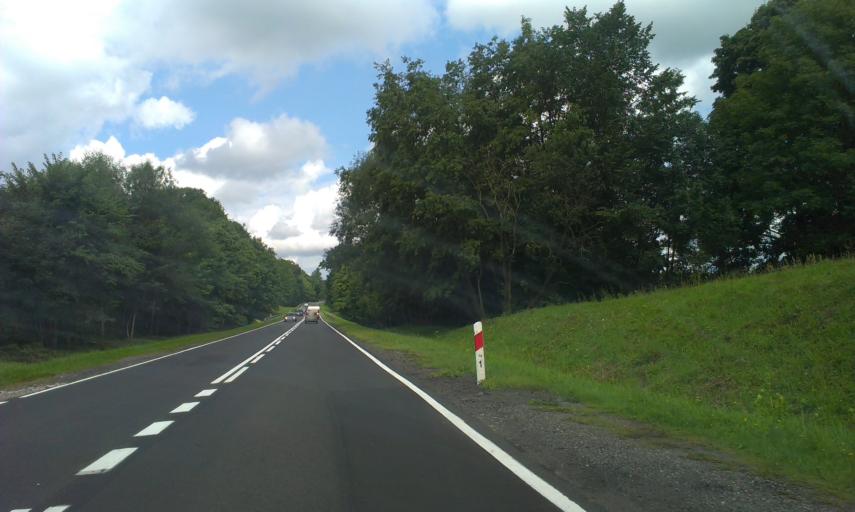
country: PL
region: West Pomeranian Voivodeship
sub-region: Powiat koszalinski
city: Bobolice
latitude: 53.9838
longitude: 16.5432
